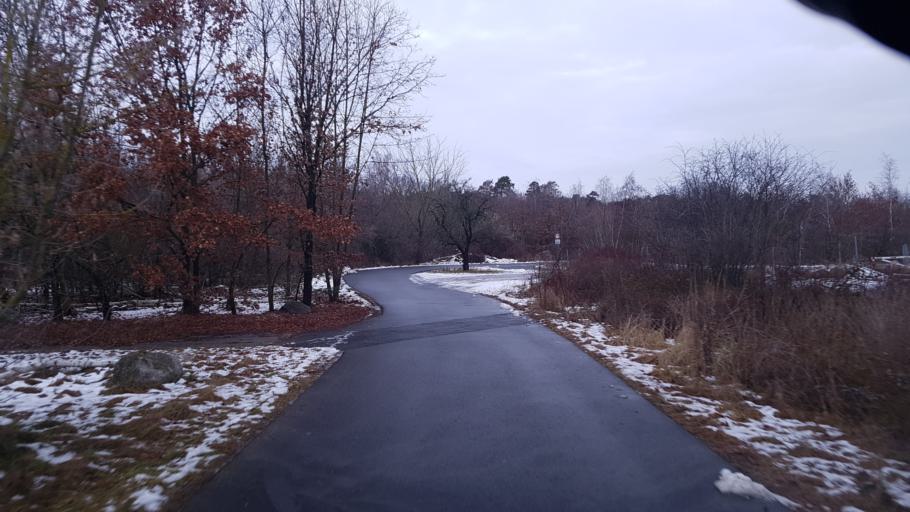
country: DE
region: Brandenburg
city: Cottbus
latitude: 51.7971
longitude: 14.3830
